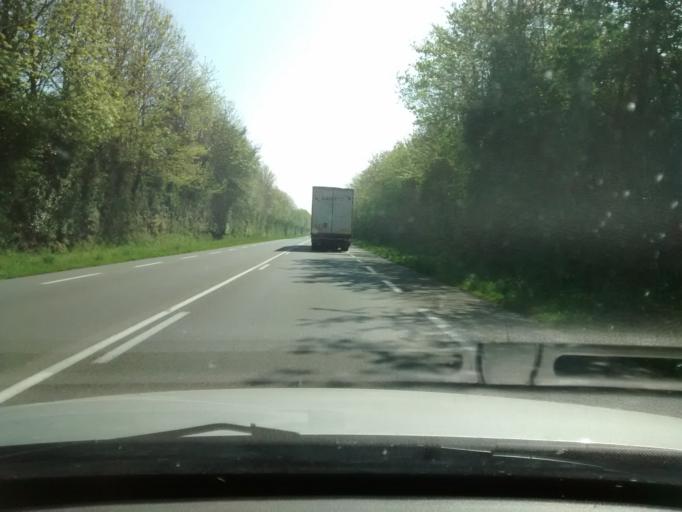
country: FR
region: Pays de la Loire
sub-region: Departement de la Mayenne
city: Bonchamp-les-Laval
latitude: 48.0696
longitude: -0.6892
